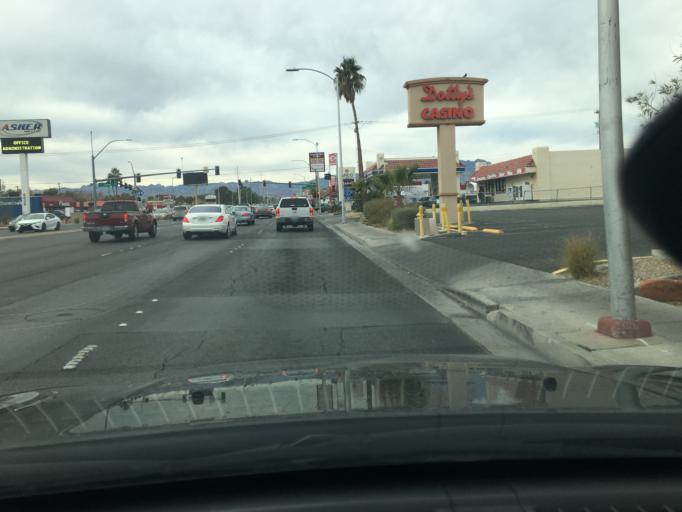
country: US
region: Nevada
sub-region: Clark County
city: Spring Valley
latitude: 36.1594
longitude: -115.2228
